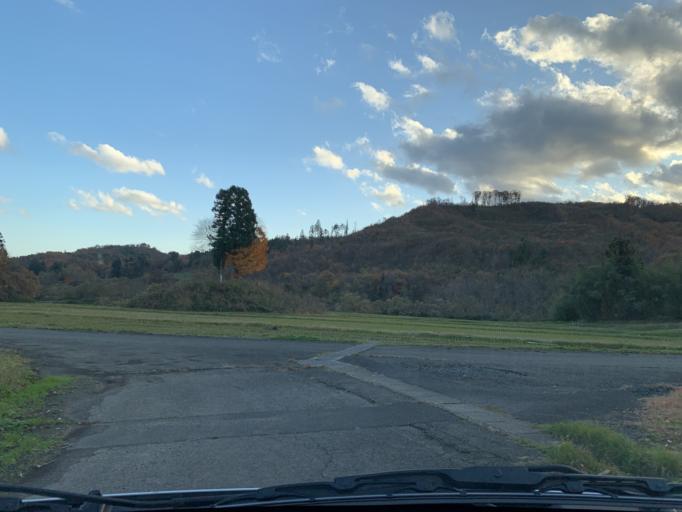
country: JP
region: Iwate
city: Mizusawa
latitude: 39.0499
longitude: 141.0431
